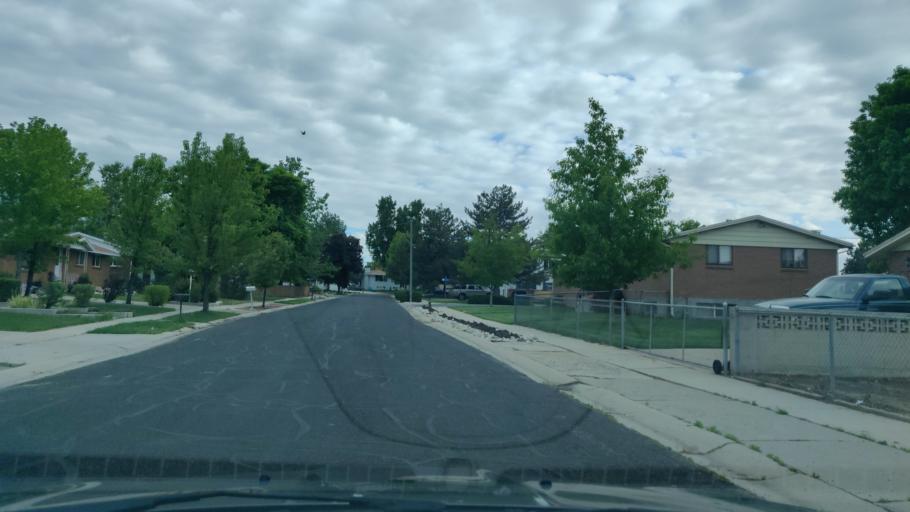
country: US
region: Utah
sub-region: Salt Lake County
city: Little Cottonwood Creek Valley
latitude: 40.6187
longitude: -111.8474
